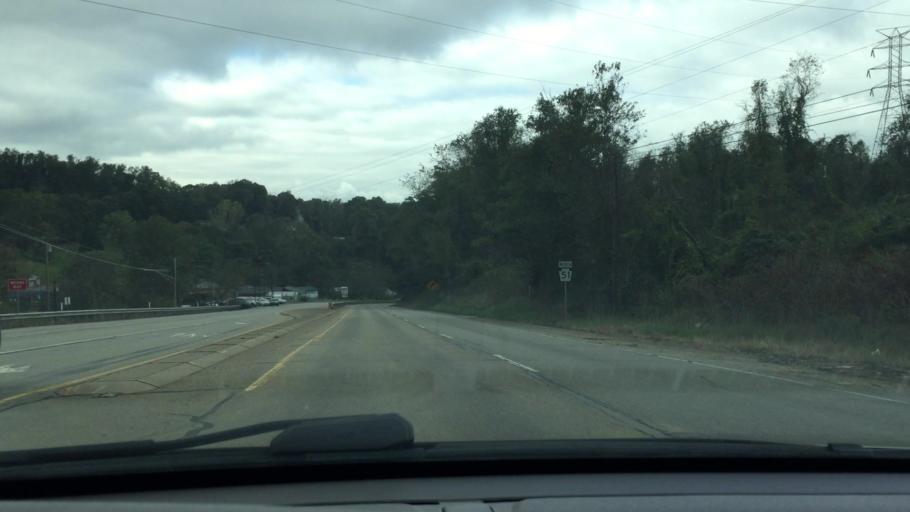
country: US
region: Pennsylvania
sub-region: Allegheny County
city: Elizabeth
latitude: 40.2392
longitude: -79.8665
